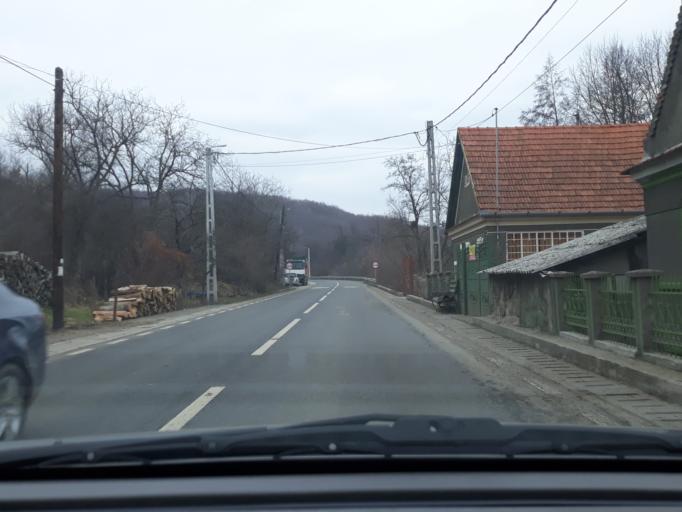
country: RO
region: Bihor
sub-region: Oras Alesd
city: Pestis
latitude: 47.0772
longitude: 22.4119
